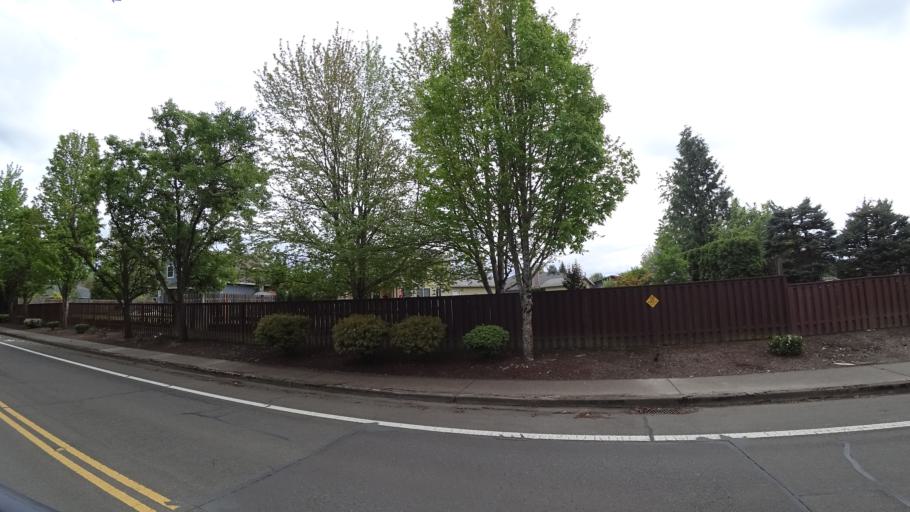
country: US
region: Oregon
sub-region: Washington County
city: Rockcreek
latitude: 45.5382
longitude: -122.9294
